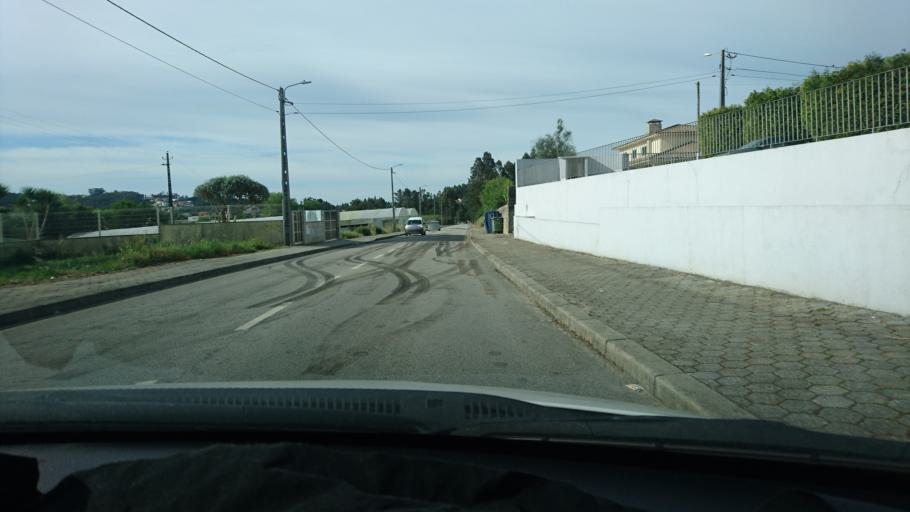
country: PT
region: Aveiro
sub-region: Oliveira de Azemeis
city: Sao Roque
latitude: 40.8784
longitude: -8.4740
